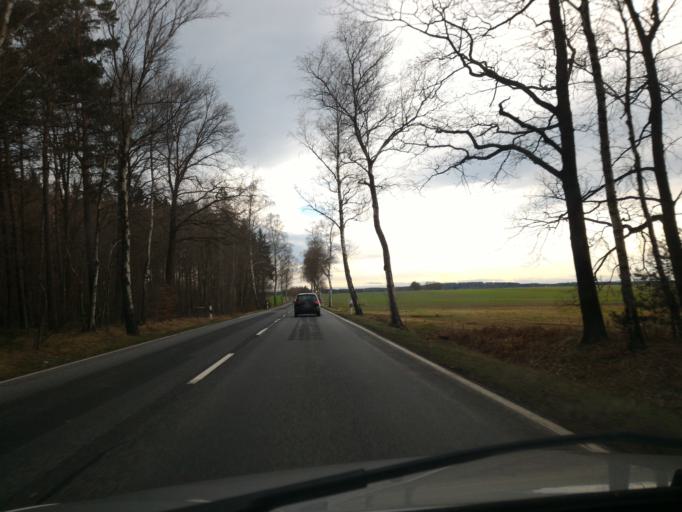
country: DE
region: Saxony
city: Stolpen
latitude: 51.0832
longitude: 14.0484
